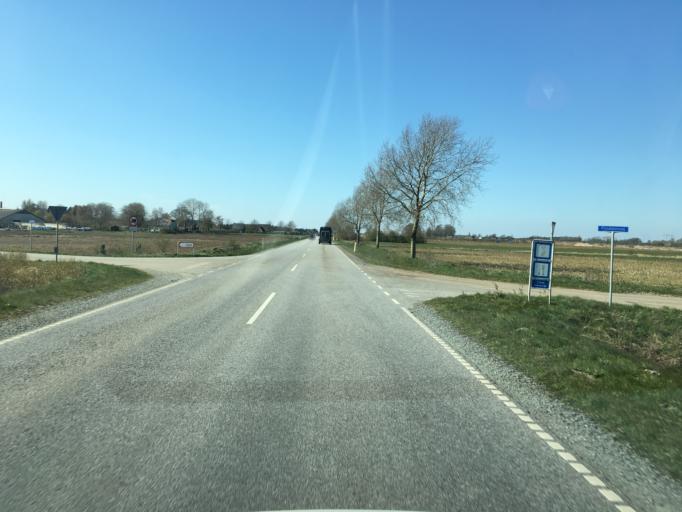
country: DK
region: South Denmark
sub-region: Aabenraa Kommune
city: Tinglev
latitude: 54.9661
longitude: 9.3191
